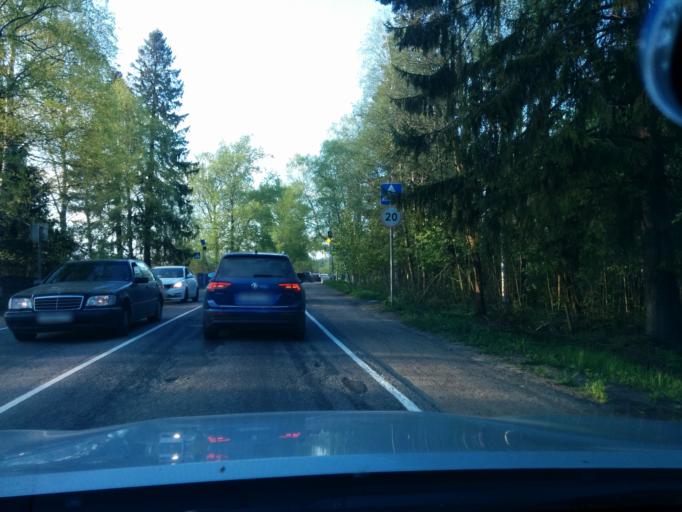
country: RU
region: Leningrad
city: Verkhniye Osel'ki
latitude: 60.2316
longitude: 30.4324
